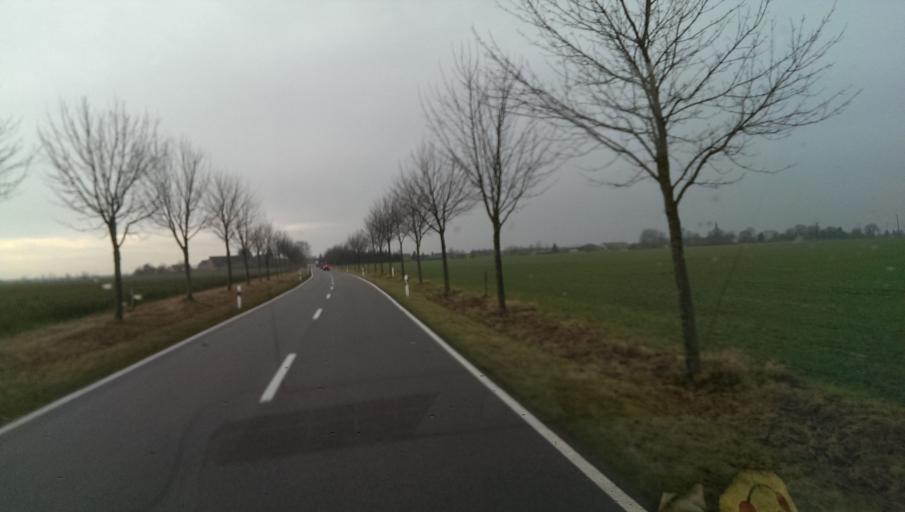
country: DE
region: Brandenburg
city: Juterbog
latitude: 51.9192
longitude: 13.1026
